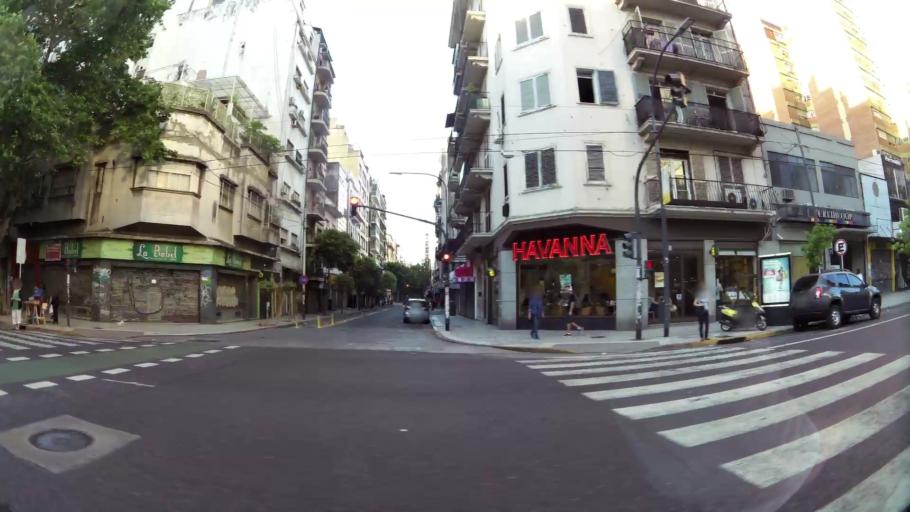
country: AR
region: Buenos Aires F.D.
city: Buenos Aires
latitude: -34.6038
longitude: -58.3976
